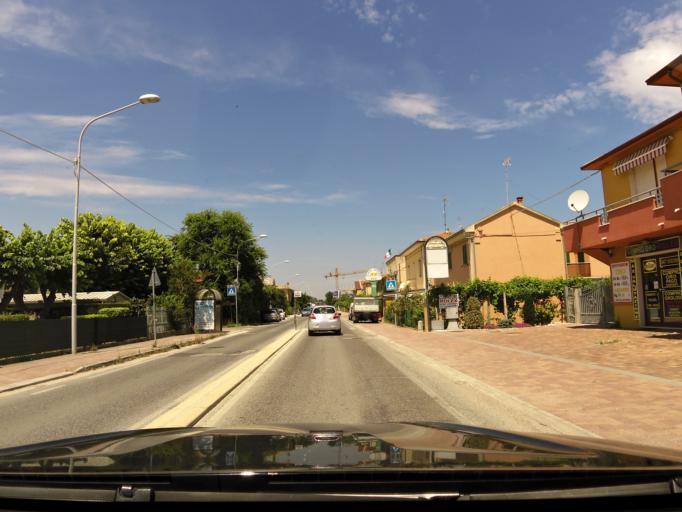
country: IT
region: The Marches
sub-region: Provincia di Pesaro e Urbino
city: Marotta
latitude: 43.7427
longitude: 13.1798
